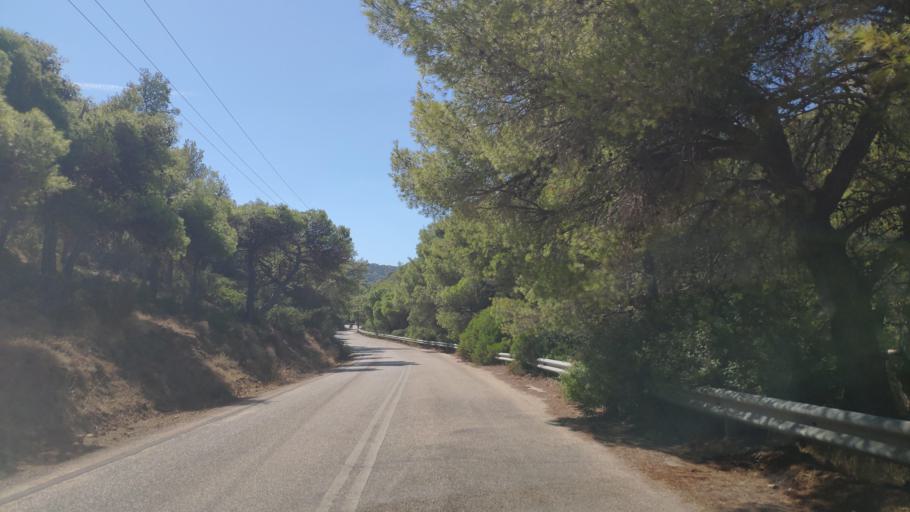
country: GR
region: Attica
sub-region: Nomarchia Anatolikis Attikis
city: Limin Mesoyaias
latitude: 37.8449
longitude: 24.0164
